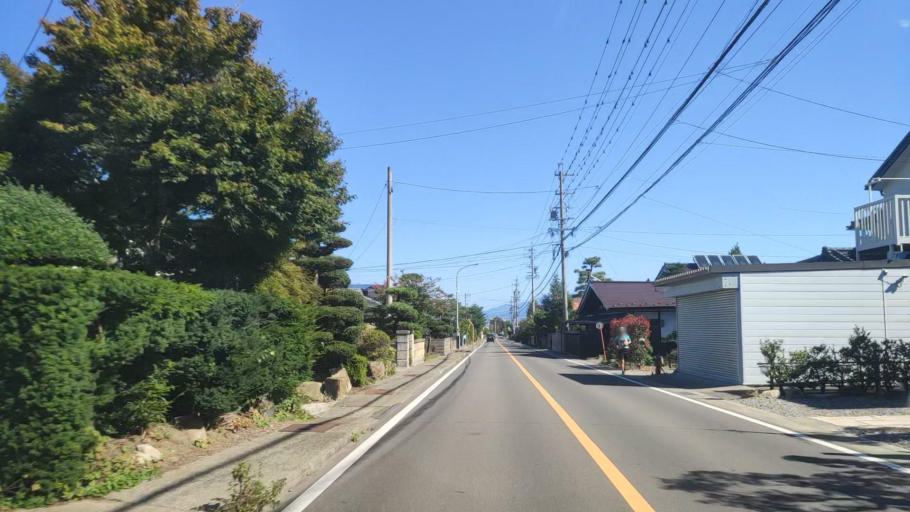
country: JP
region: Nagano
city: Shiojiri
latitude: 36.1367
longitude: 137.9379
